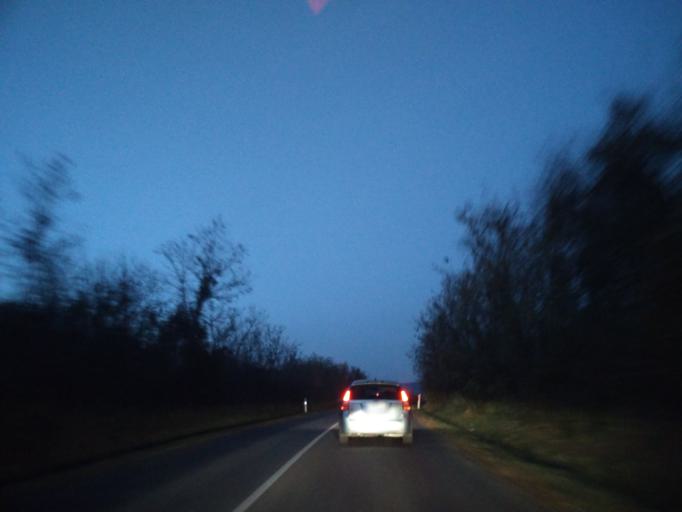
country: HU
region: Pest
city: Budakeszi
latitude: 47.4838
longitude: 18.9056
